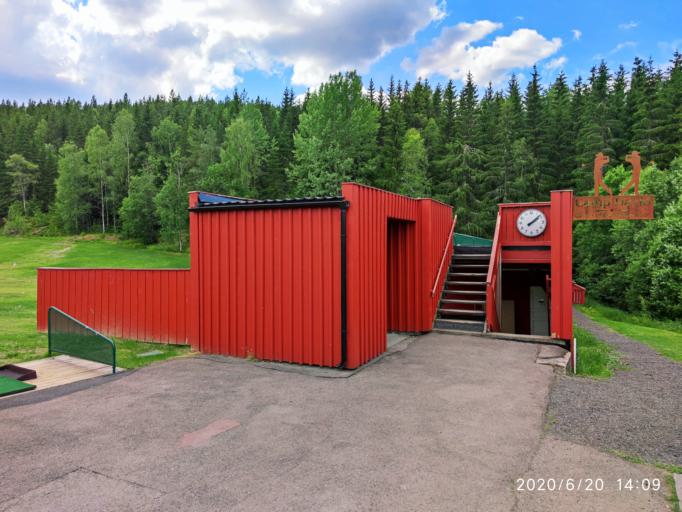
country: NO
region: Akershus
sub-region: Lorenskog
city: Kjenn
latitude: 59.8871
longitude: 10.9801
